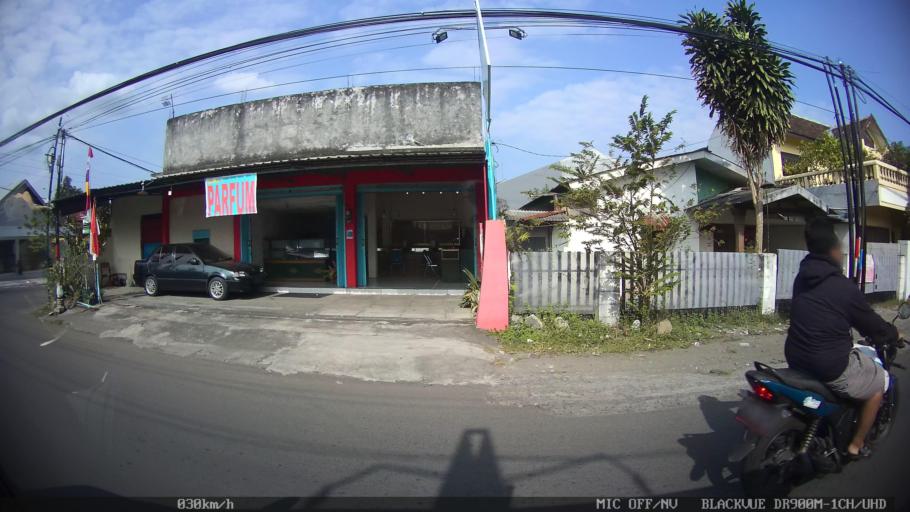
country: ID
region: Daerah Istimewa Yogyakarta
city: Depok
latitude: -7.7510
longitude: 110.4488
